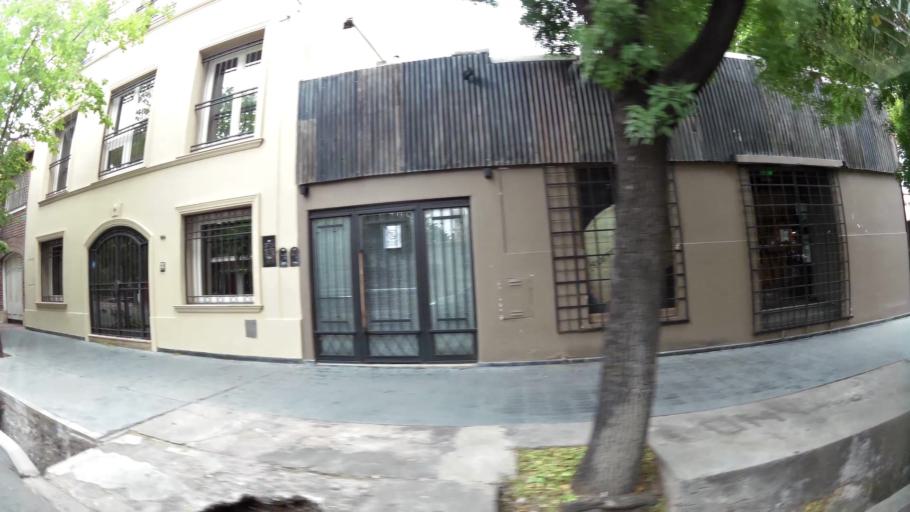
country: AR
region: Mendoza
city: Mendoza
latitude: -32.8851
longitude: -68.8605
